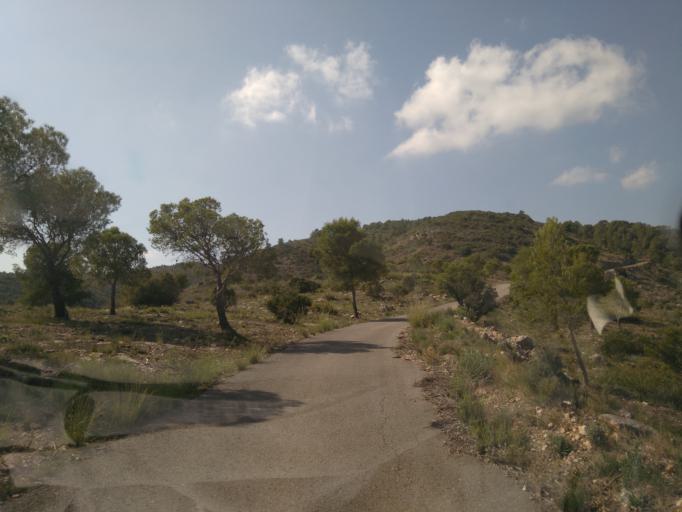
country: ES
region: Valencia
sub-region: Provincia de Valencia
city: Tous
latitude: 39.1742
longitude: -0.6094
